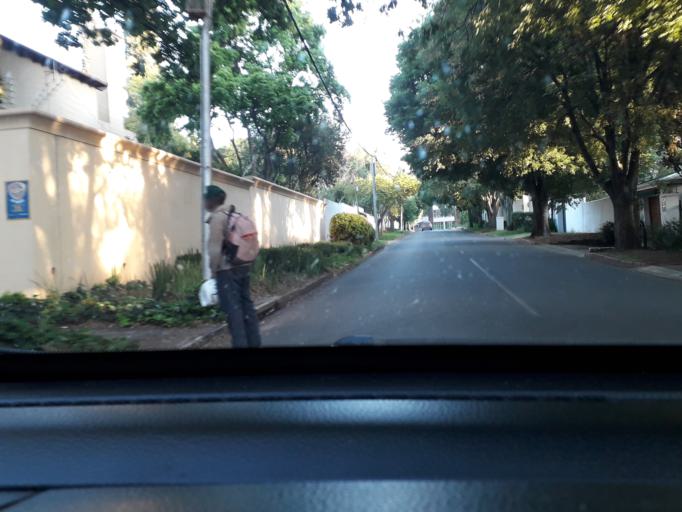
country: ZA
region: Gauteng
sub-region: City of Johannesburg Metropolitan Municipality
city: Johannesburg
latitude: -26.1379
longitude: 28.0526
